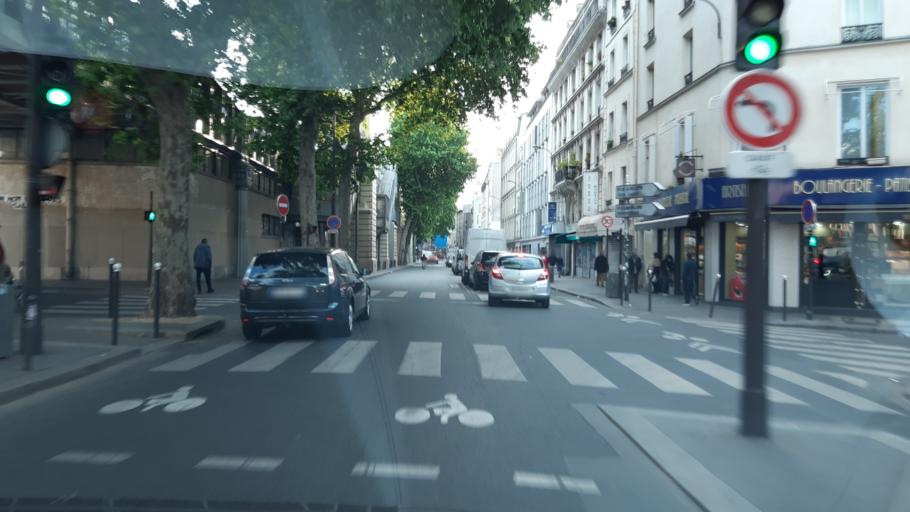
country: FR
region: Ile-de-France
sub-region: Paris
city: Paris
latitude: 48.8844
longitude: 2.3672
